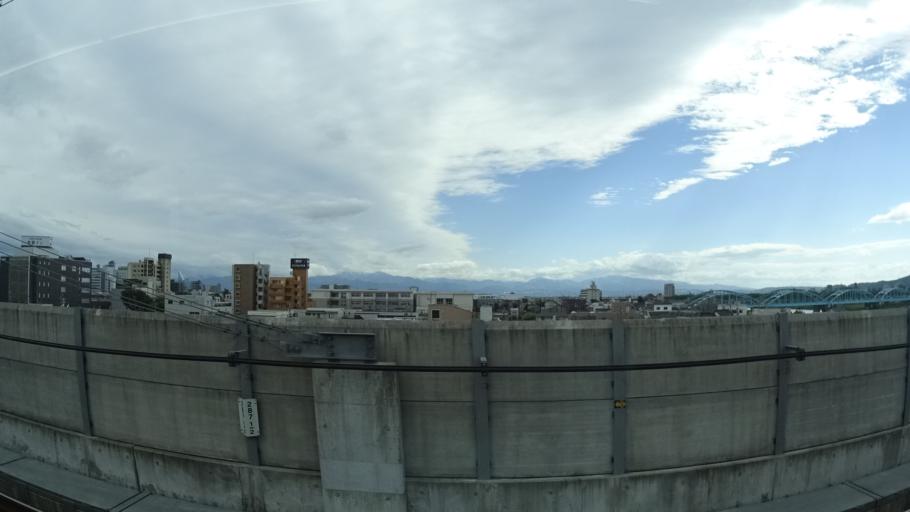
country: JP
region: Toyama
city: Toyama-shi
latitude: 36.7039
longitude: 137.2071
